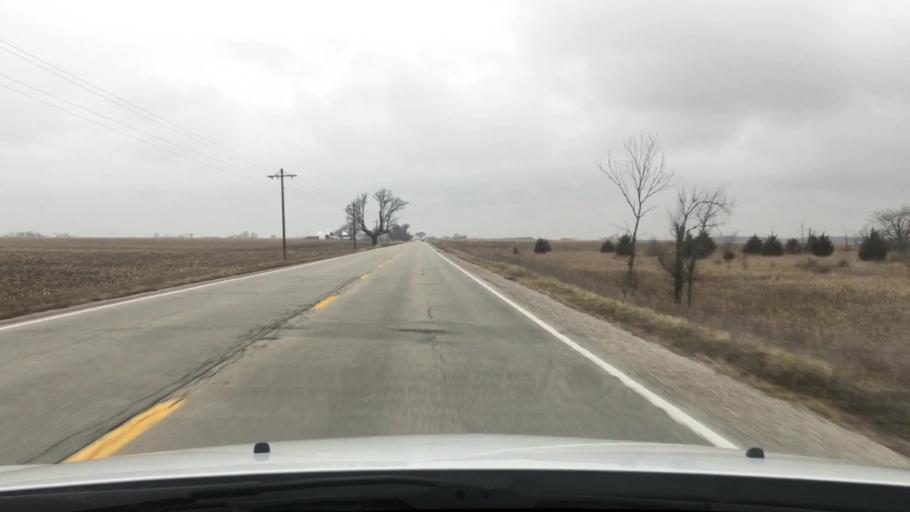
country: US
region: Illinois
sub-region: Iroquois County
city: Clifton
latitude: 40.8877
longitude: -87.8345
